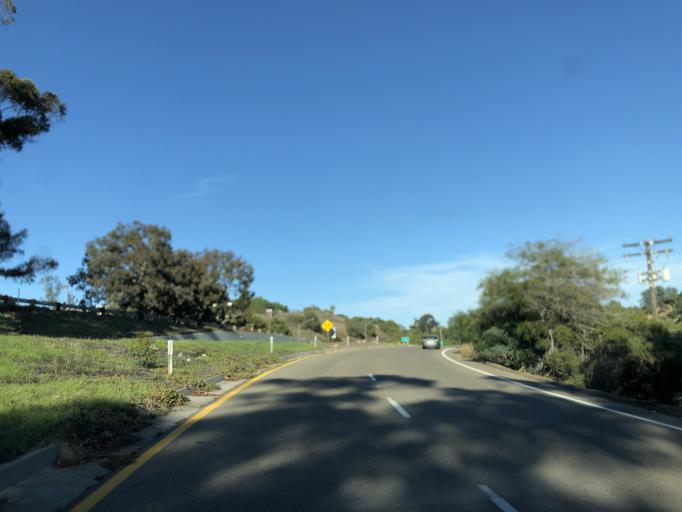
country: US
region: California
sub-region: San Diego County
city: San Diego
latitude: 32.7189
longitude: -117.1467
